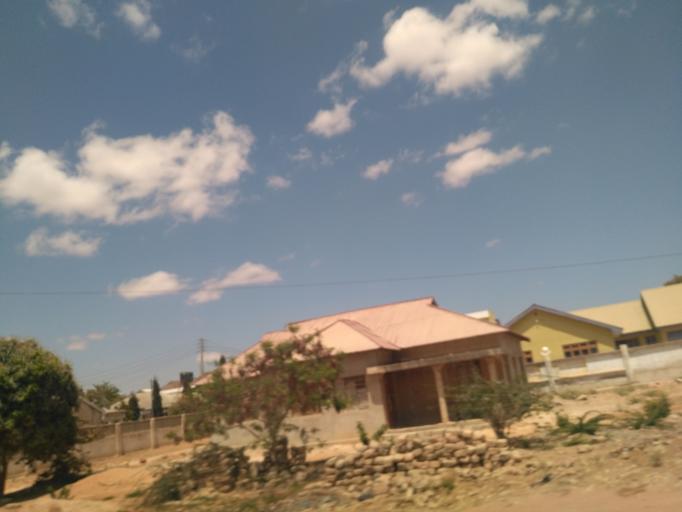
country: TZ
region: Dodoma
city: Kisasa
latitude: -6.1682
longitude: 35.7737
